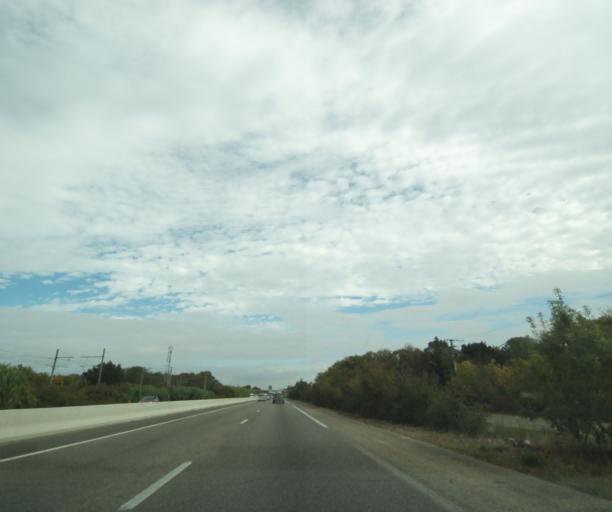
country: FR
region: Provence-Alpes-Cote d'Azur
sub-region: Departement des Bouches-du-Rhone
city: Arles
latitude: 43.6437
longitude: 4.7054
